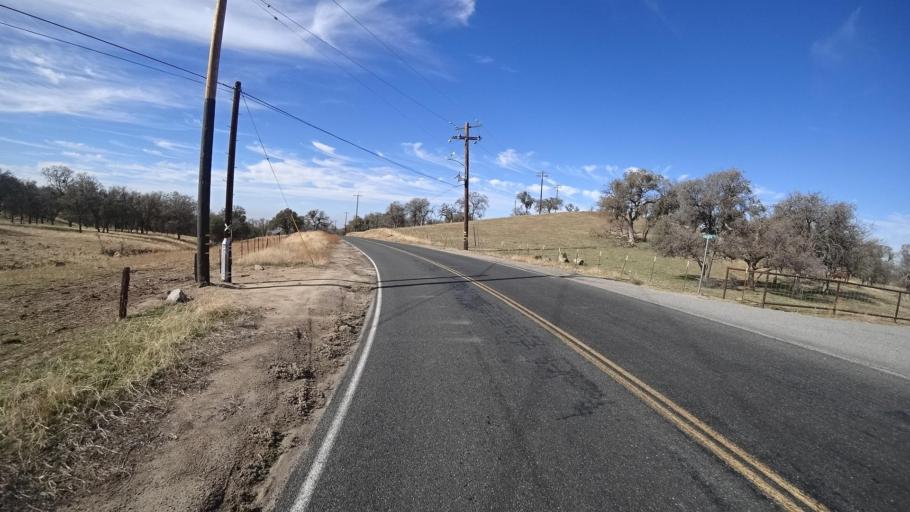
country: US
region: California
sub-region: Kern County
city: Alta Sierra
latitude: 35.6470
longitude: -118.7896
